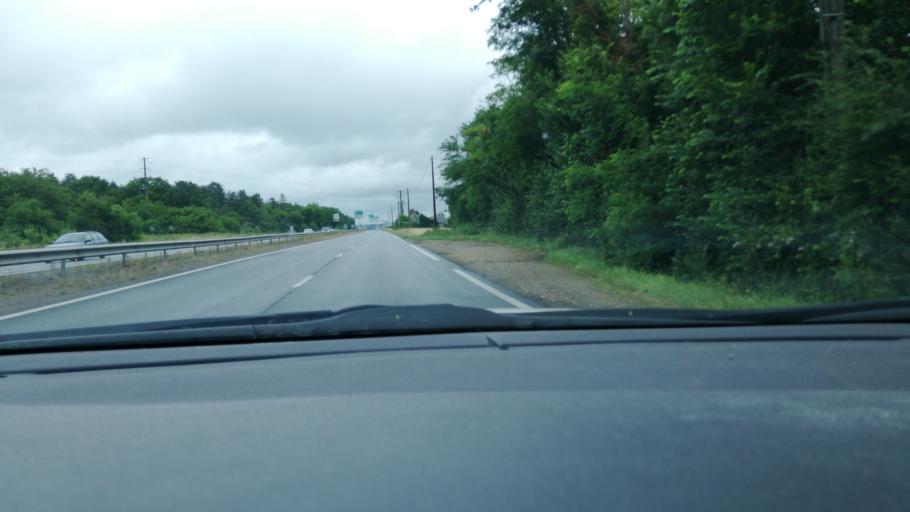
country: FR
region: Poitou-Charentes
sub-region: Departement de la Vienne
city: Cenon-sur-Vienne
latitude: 46.7746
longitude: 0.5131
